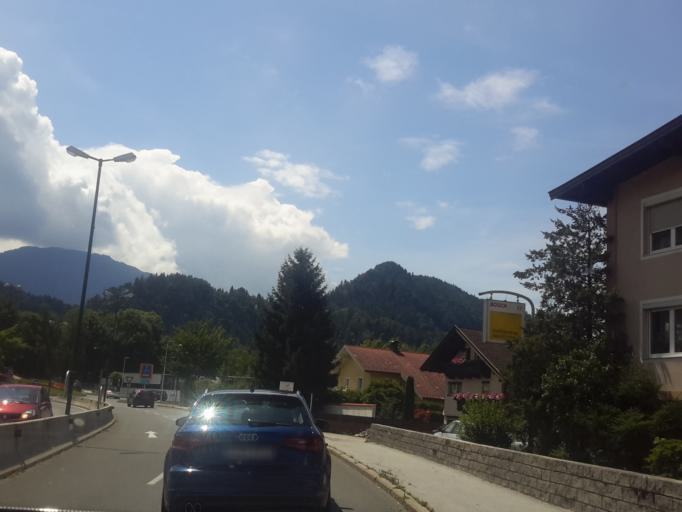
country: AT
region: Tyrol
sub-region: Politischer Bezirk Kufstein
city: Kufstein
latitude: 47.5734
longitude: 12.1567
